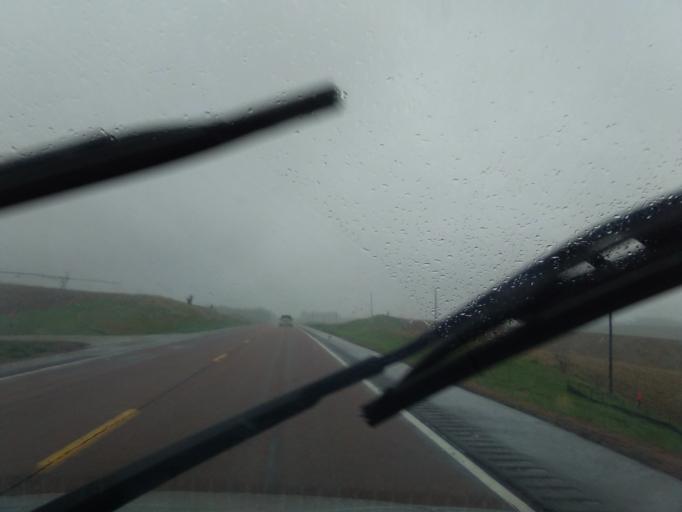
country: US
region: Nebraska
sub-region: Wayne County
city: Wayne
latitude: 42.2355
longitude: -97.1377
